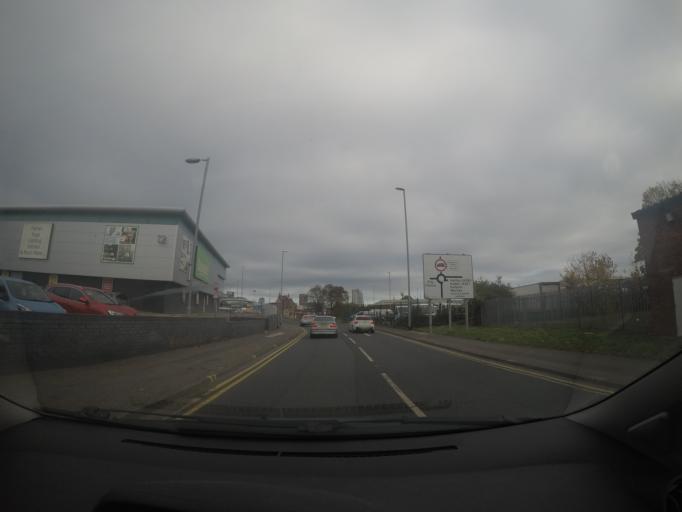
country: GB
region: England
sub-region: City and Borough of Leeds
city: Leeds
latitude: 53.7898
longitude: -1.5664
